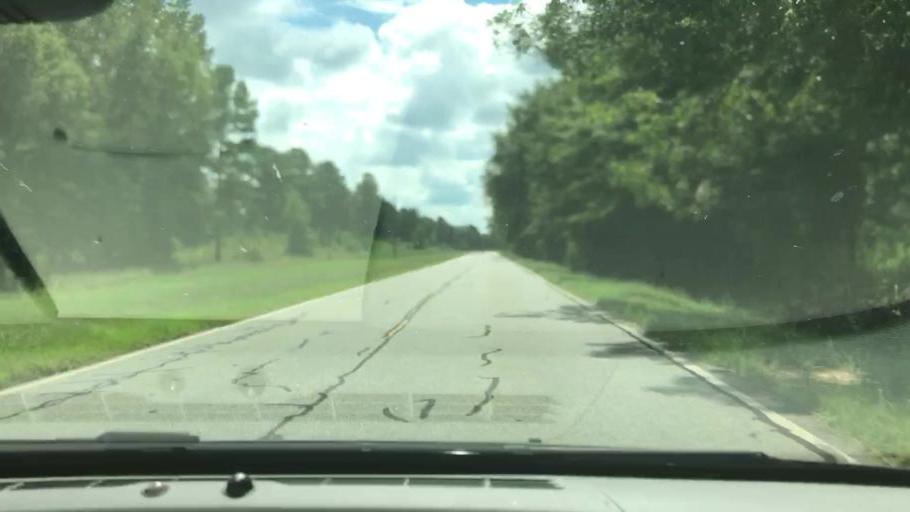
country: US
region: Georgia
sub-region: Quitman County
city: Georgetown
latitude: 32.1088
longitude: -85.0381
